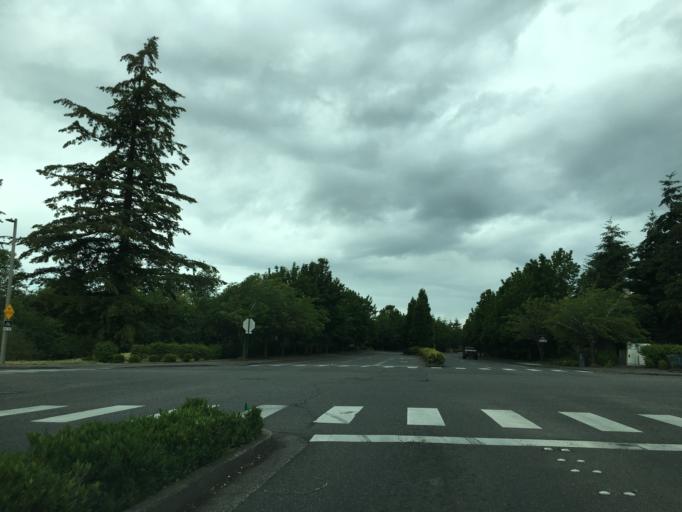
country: US
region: Washington
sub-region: Whatcom County
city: Bellingham
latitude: 48.8058
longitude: -122.4965
